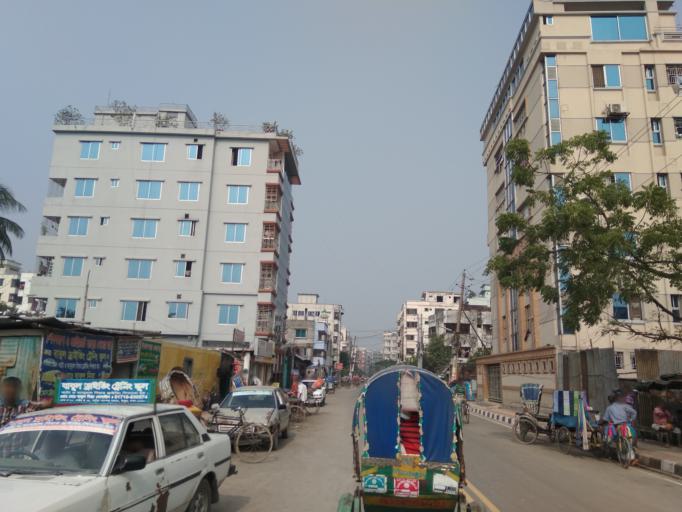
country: BD
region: Dhaka
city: Tungi
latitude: 23.8646
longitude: 90.3858
